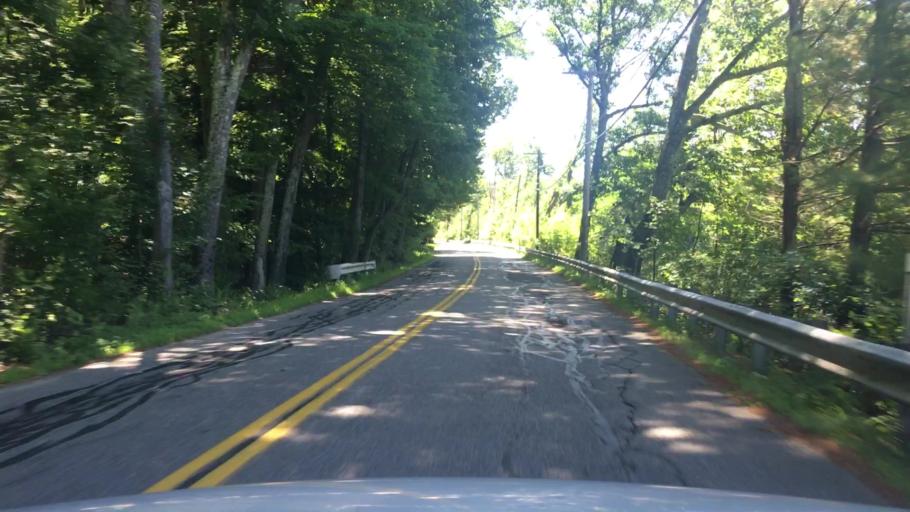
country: US
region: New Hampshire
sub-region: Merrimack County
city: Boscawen
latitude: 43.2548
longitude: -71.6209
